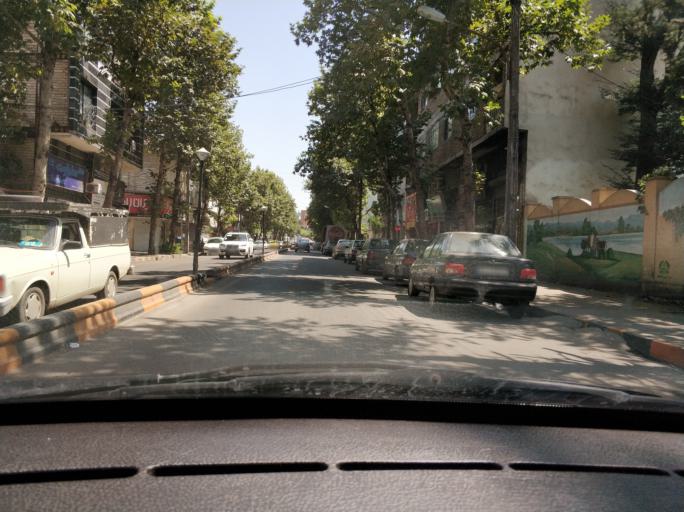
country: IR
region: Gilan
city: Lahijan
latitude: 37.1985
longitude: 50.0110
